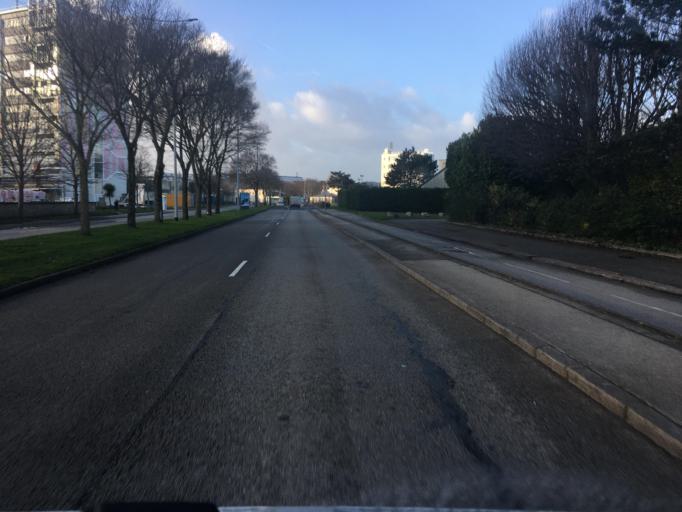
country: FR
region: Lower Normandy
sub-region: Departement de la Manche
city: Cherbourg-Octeville
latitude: 49.6451
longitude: -1.6292
